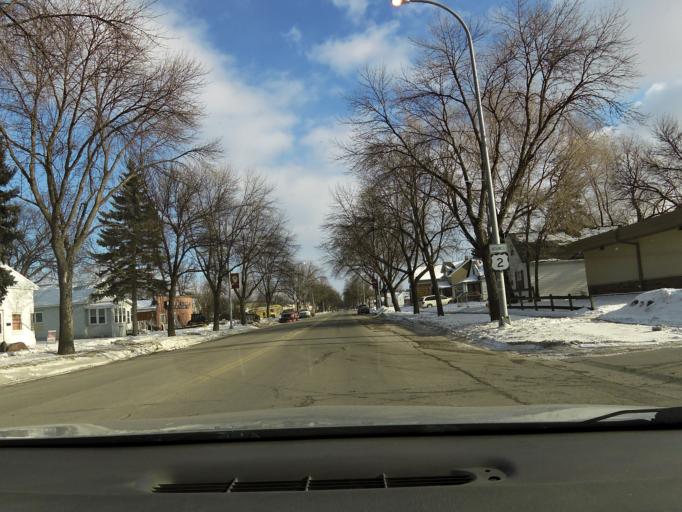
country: US
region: North Dakota
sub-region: Grand Forks County
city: Grand Forks
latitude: 47.9327
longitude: -97.0485
